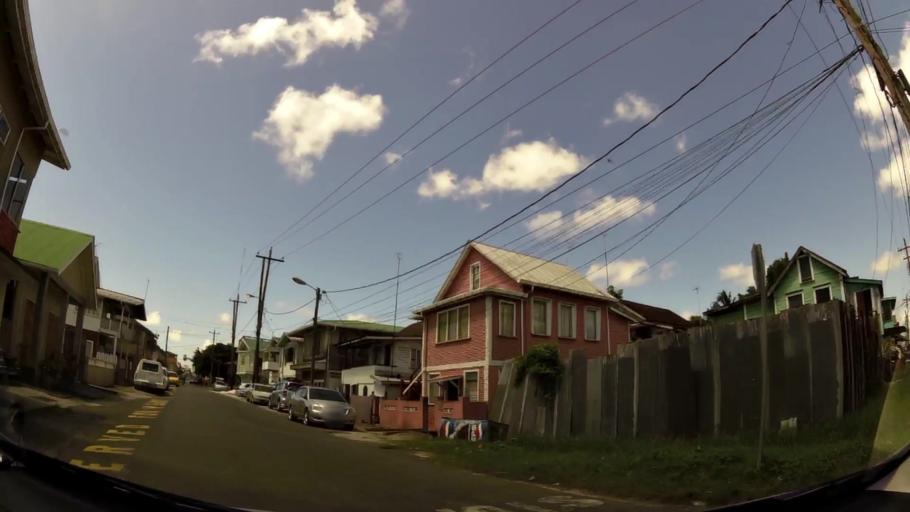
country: GY
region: Demerara-Mahaica
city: Georgetown
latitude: 6.8042
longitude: -58.1610
